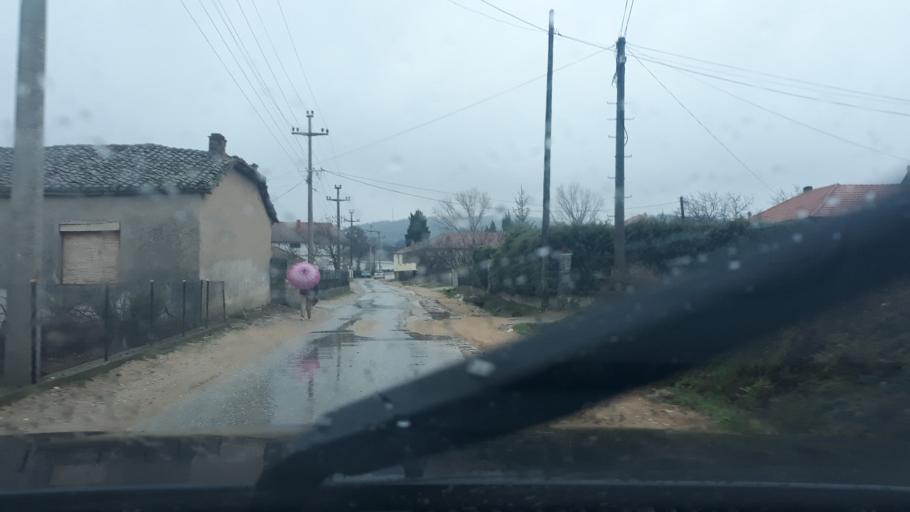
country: MK
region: Bogdanci
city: Bogdanci
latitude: 41.2430
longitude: 22.6129
